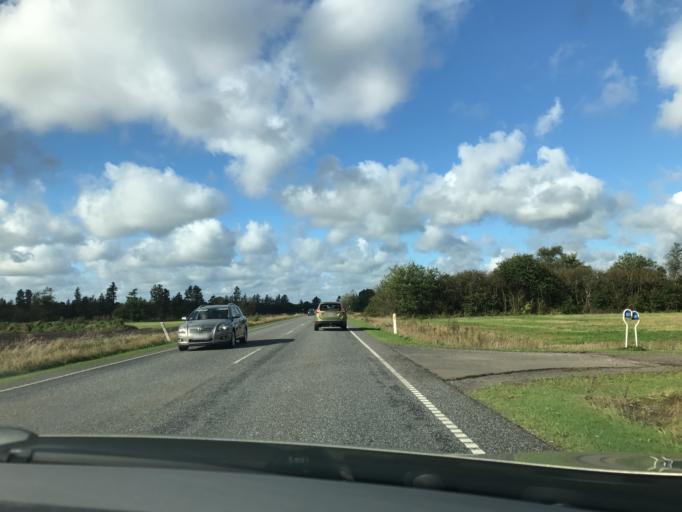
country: DK
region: South Denmark
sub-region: Billund Kommune
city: Billund
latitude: 55.7200
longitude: 9.1652
